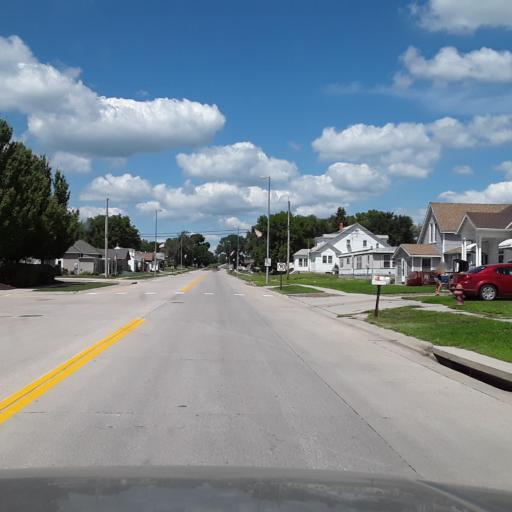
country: US
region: Nebraska
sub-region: Nance County
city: Genoa
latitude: 41.4492
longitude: -97.7256
